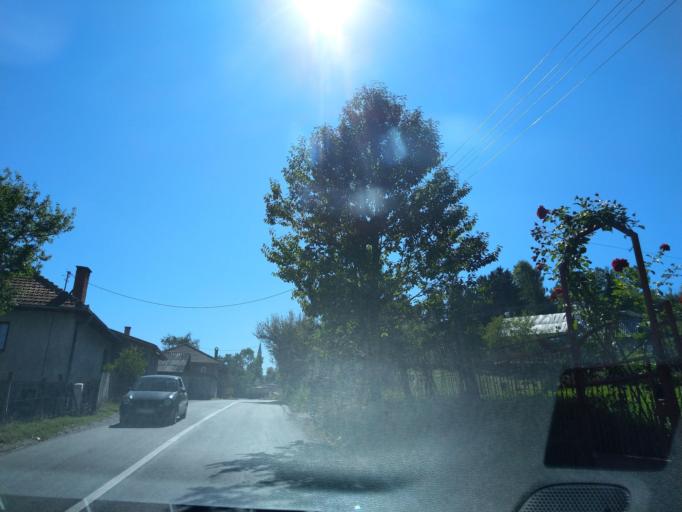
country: RS
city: Sokolovica
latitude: 43.2513
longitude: 20.2280
